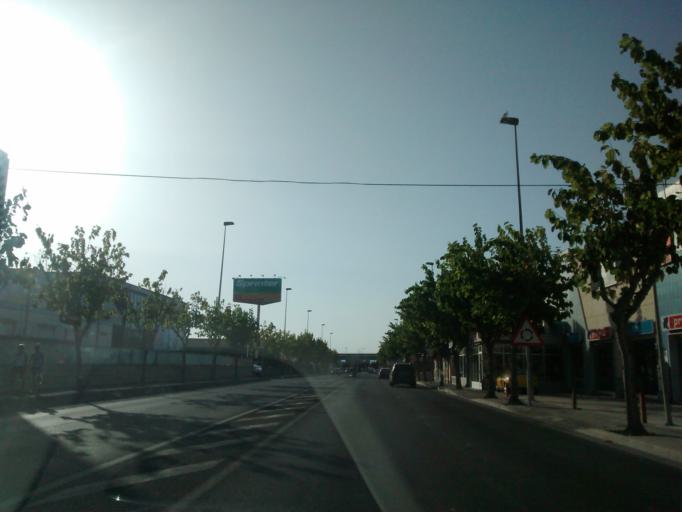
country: ES
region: Valencia
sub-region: Provincia de Alicante
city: Santa Pola
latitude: 38.1986
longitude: -0.5659
